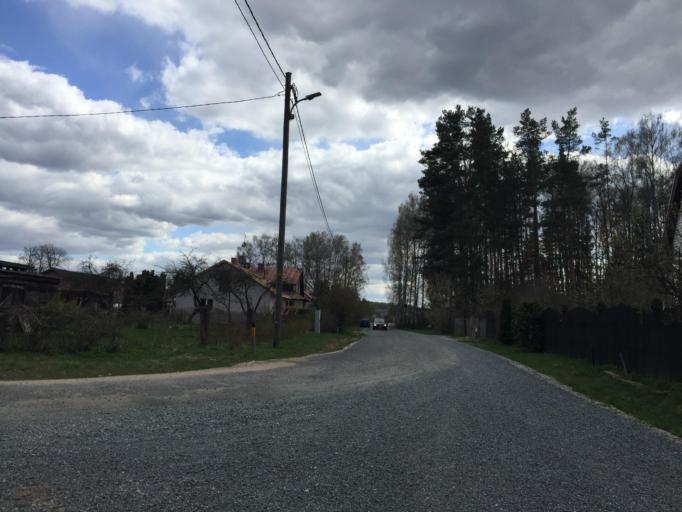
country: LV
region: Baldone
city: Baldone
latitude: 56.7495
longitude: 24.3882
